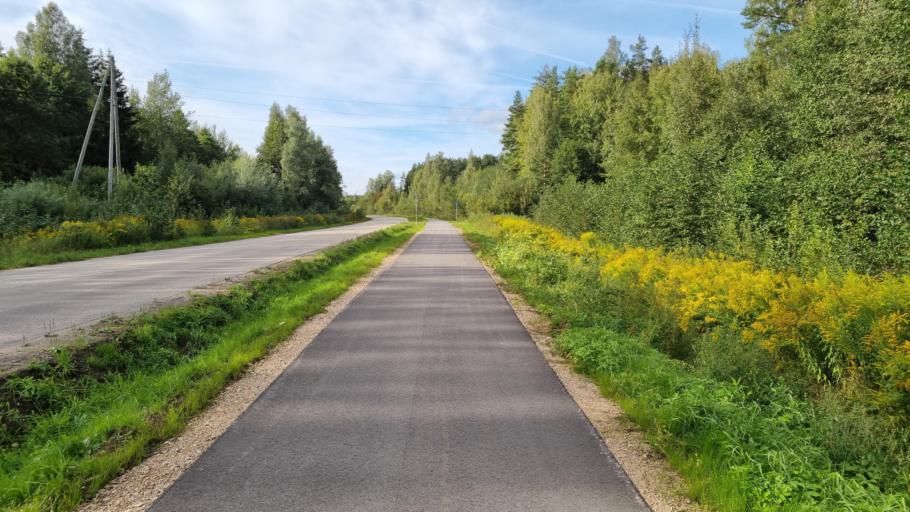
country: LV
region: Lecava
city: Iecava
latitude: 56.6952
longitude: 24.0868
